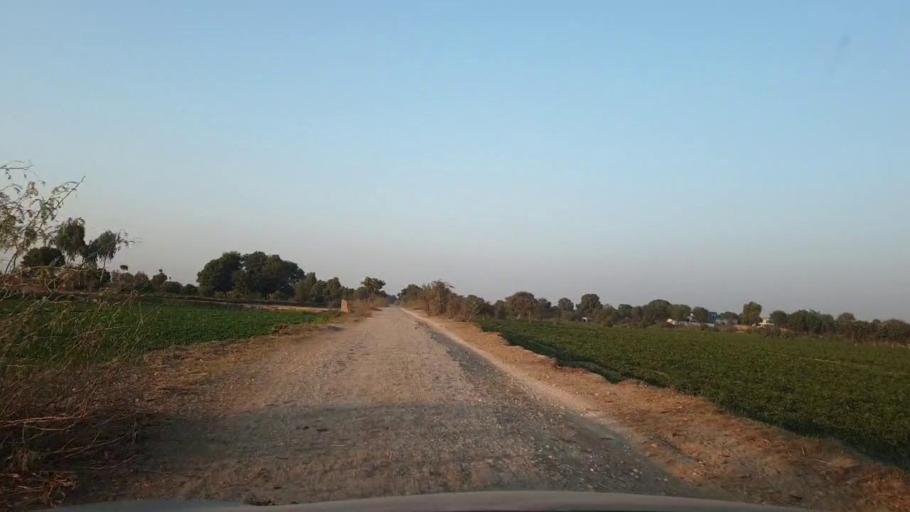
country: PK
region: Sindh
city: Tando Allahyar
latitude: 25.5038
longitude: 68.7405
